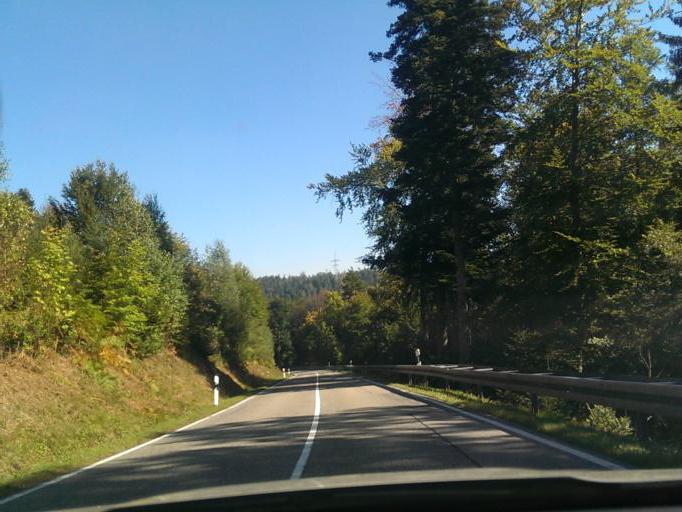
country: DE
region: Baden-Wuerttemberg
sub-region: Karlsruhe Region
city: Hofen an der Enz
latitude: 48.7999
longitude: 8.5442
